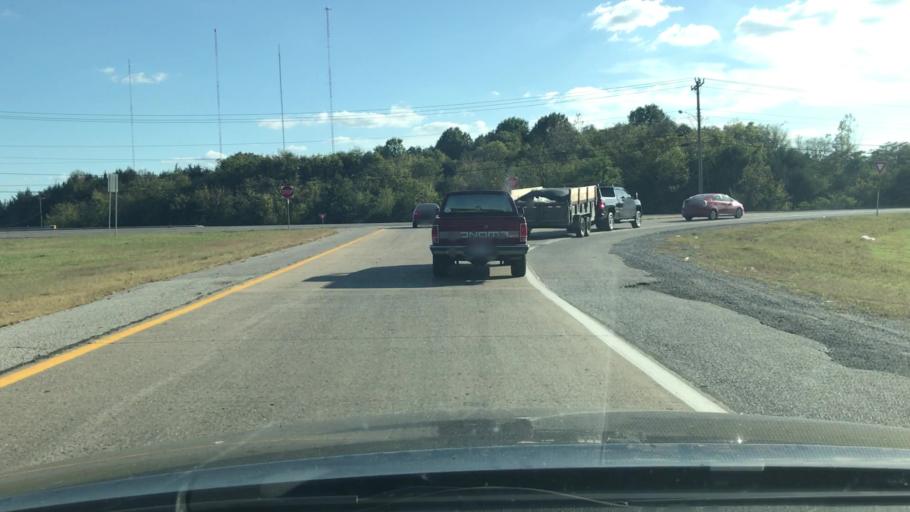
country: US
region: Tennessee
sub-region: Davidson County
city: Nashville
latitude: 36.2106
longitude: -86.8726
